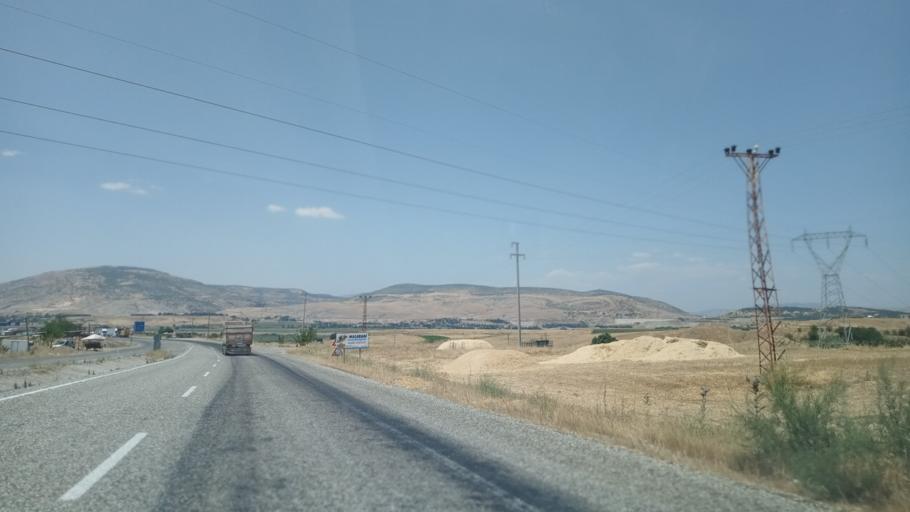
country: TR
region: Diyarbakir
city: Malabadi
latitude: 38.1347
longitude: 41.2367
